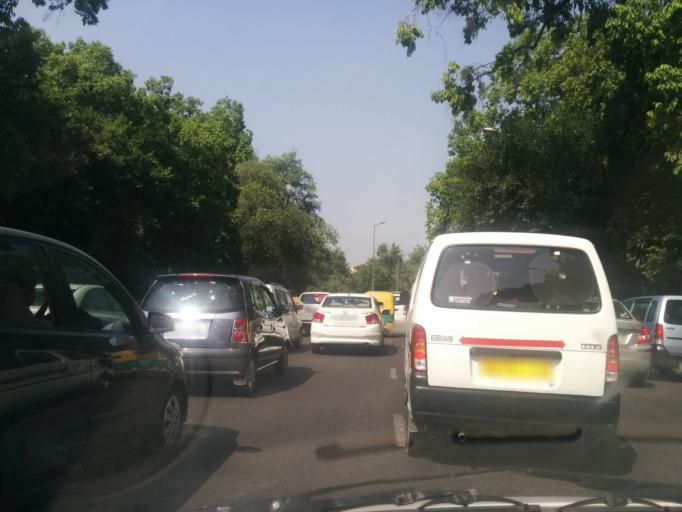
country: IN
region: NCT
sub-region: New Delhi
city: New Delhi
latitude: 28.6098
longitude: 77.2318
